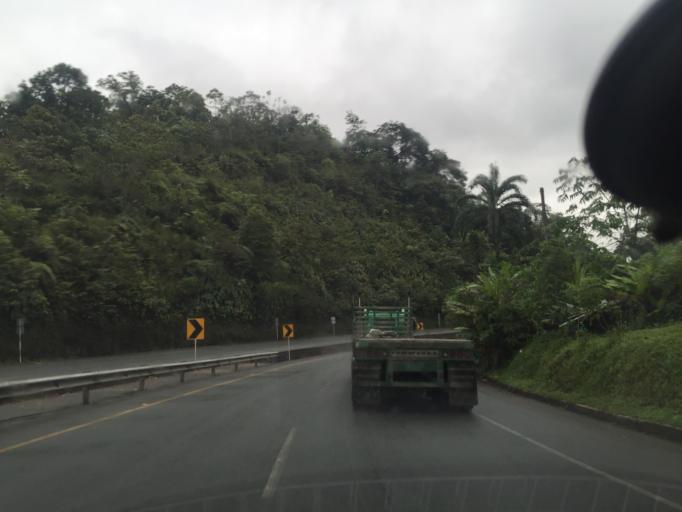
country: CO
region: Valle del Cauca
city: Buenaventura
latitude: 3.8741
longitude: -76.8555
